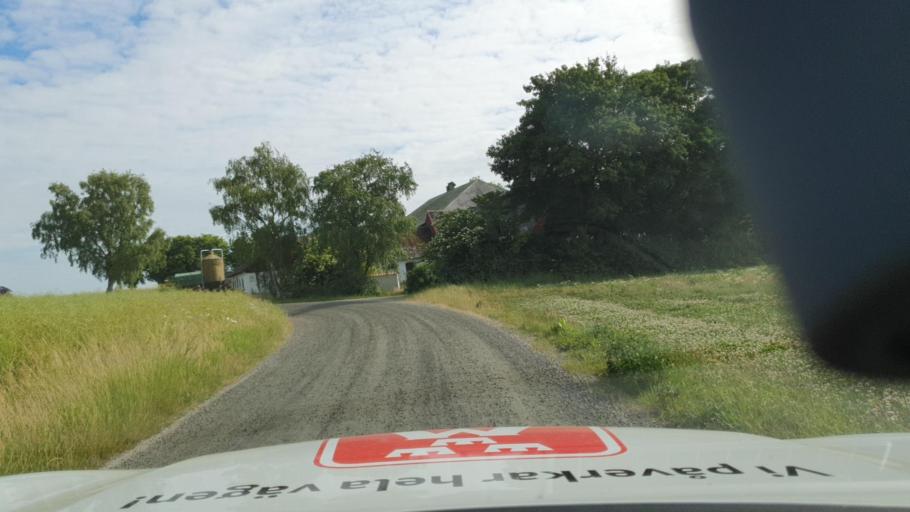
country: SE
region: Skane
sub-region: Skurups Kommun
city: Rydsgard
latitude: 55.4400
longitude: 13.5946
